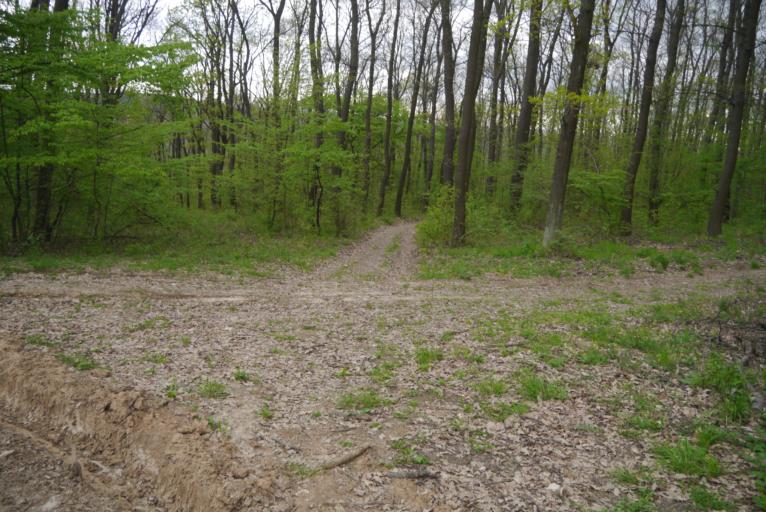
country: HU
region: Komarom-Esztergom
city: Piliscsev
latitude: 47.6836
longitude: 18.8472
